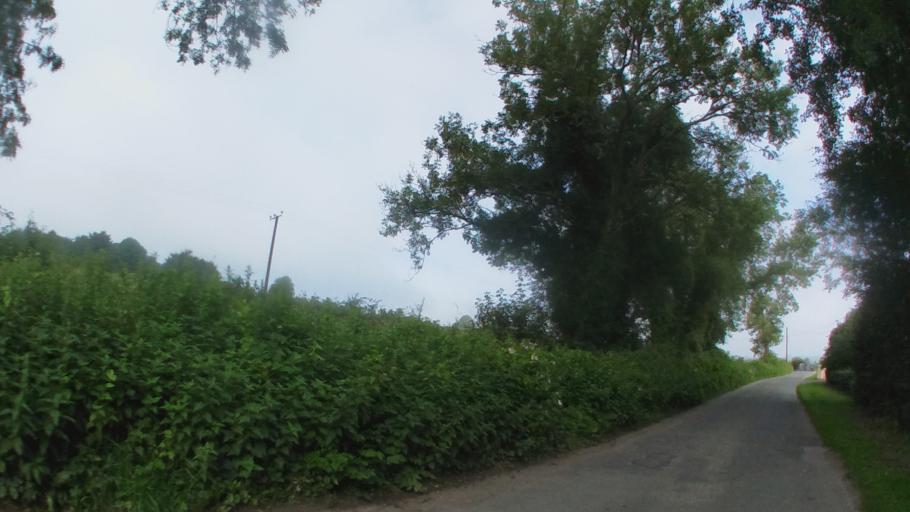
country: IE
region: Leinster
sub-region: Kilkenny
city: Kilkenny
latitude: 52.6918
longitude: -7.1891
